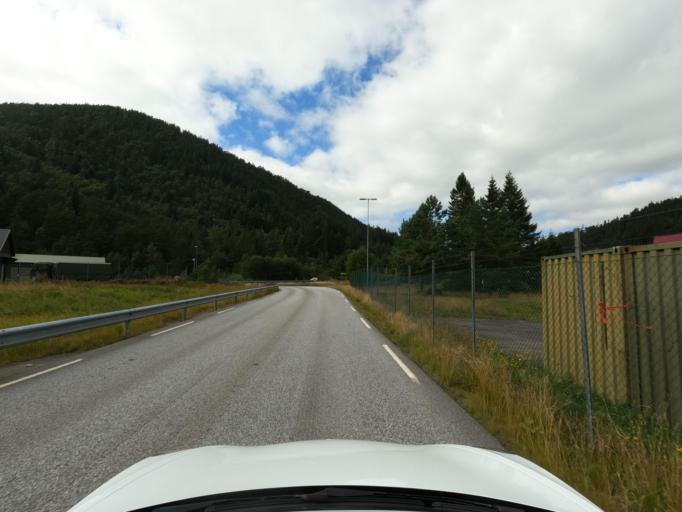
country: NO
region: Hordaland
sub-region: Os
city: Hagavik
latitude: 60.1992
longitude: 5.4223
